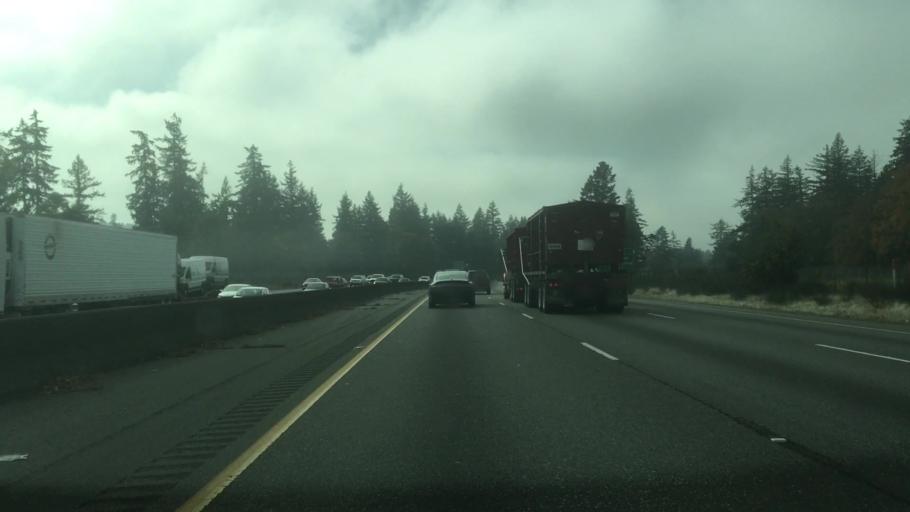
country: US
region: Washington
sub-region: Pierce County
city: Fort Lewis
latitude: 47.1116
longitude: -122.5692
